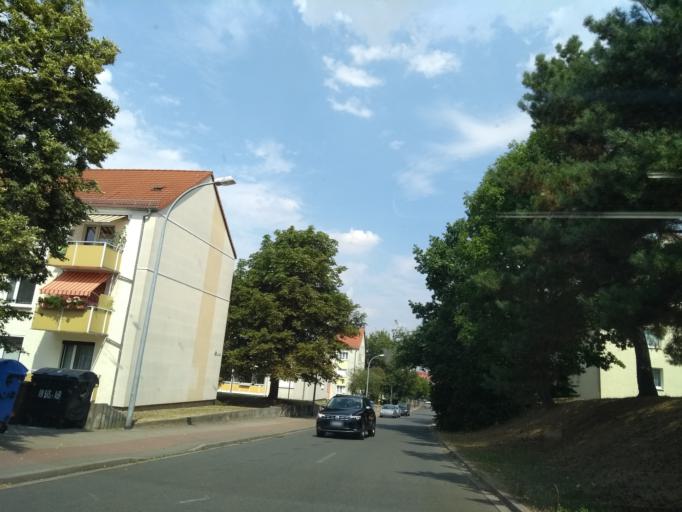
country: DE
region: Saxony-Anhalt
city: Zeitz
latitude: 51.0417
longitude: 12.1192
